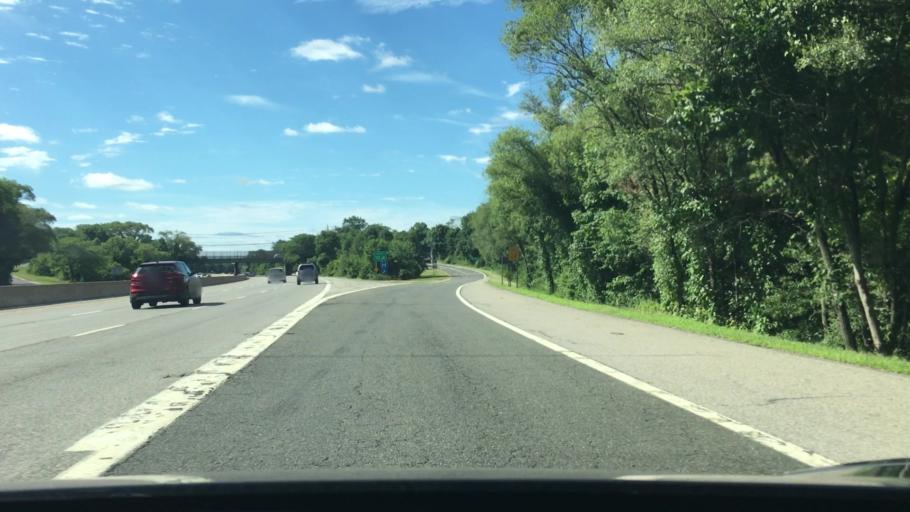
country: US
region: New York
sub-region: Nassau County
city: Plainview
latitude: 40.7764
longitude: -73.4823
